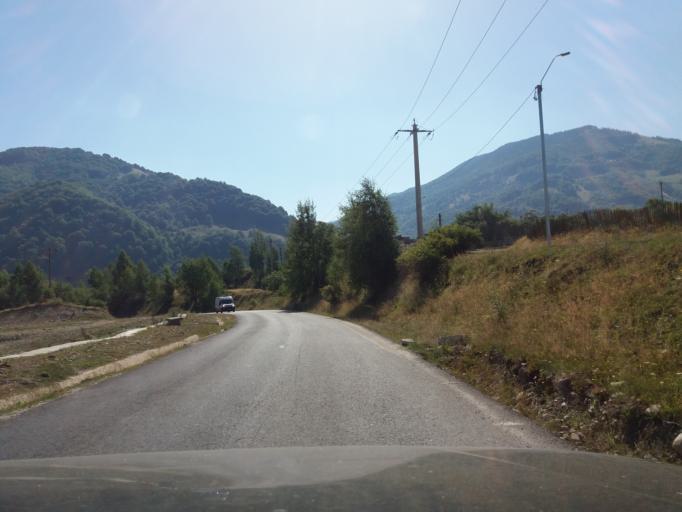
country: RO
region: Hunedoara
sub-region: Oras Petrila
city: Petrila
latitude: 45.4205
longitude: 23.4227
